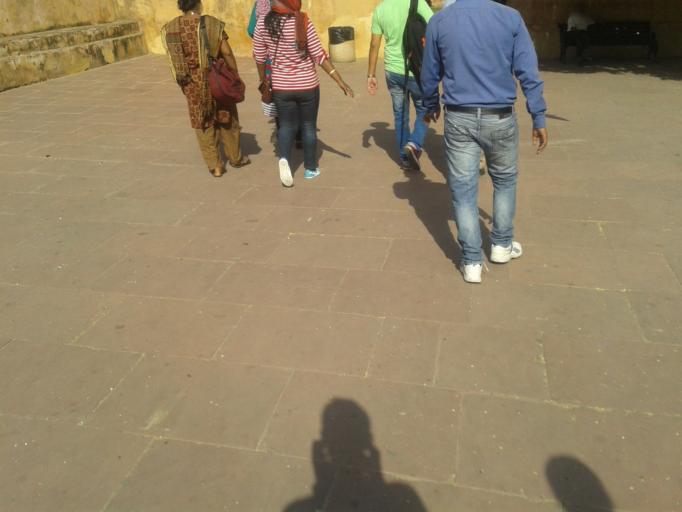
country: IN
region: Rajasthan
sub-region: Jaipur
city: Jaipur
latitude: 26.9858
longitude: 75.8538
